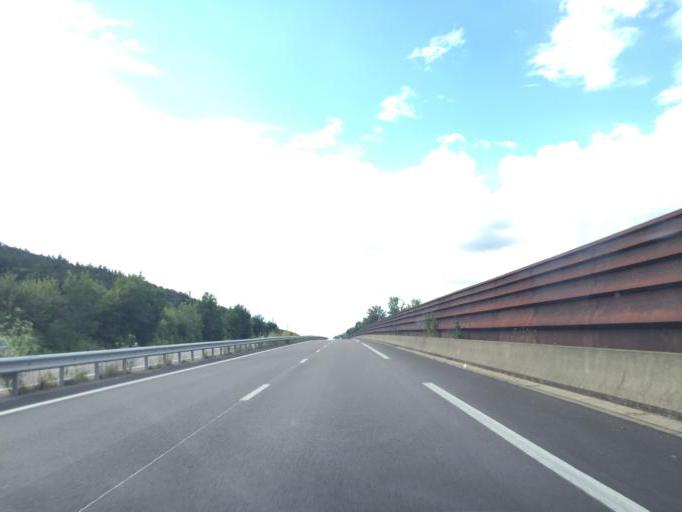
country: FR
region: Bourgogne
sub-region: Departement de Saone-et-Loire
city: La Roche-Vineuse
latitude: 46.3428
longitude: 4.7182
